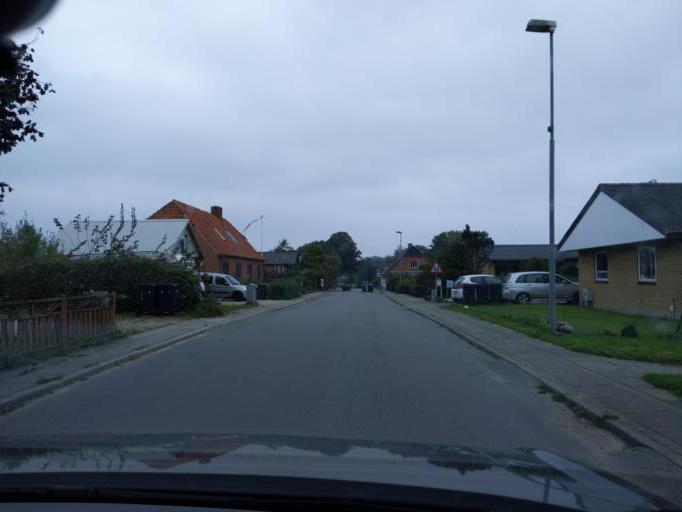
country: DK
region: Central Jutland
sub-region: Viborg Kommune
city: Stoholm
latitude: 56.4734
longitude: 9.2279
